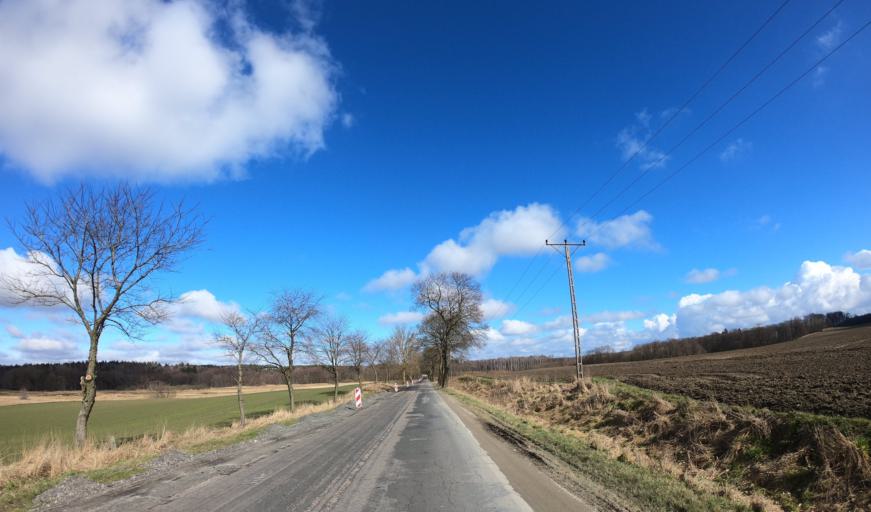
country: PL
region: West Pomeranian Voivodeship
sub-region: Powiat bialogardzki
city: Karlino
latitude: 53.9461
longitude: 15.8544
